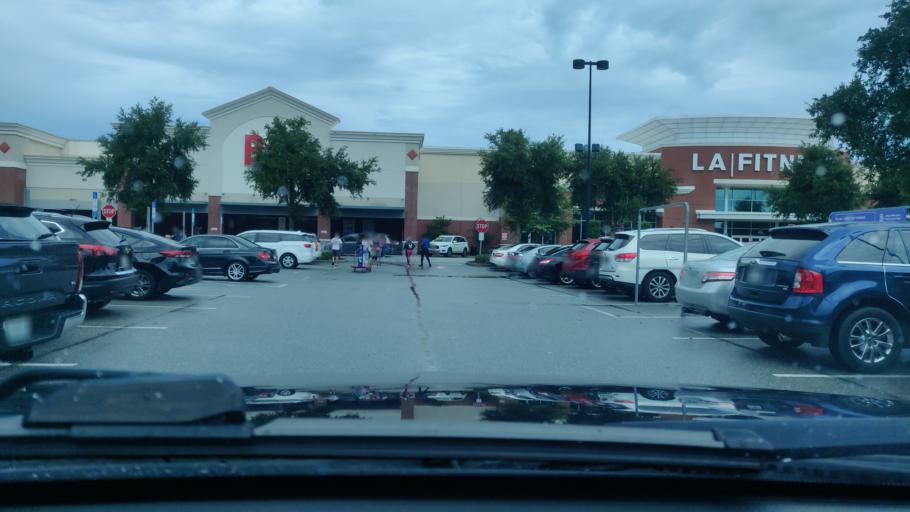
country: US
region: Florida
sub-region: Volusia County
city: Port Orange
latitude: 29.1086
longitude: -81.0248
